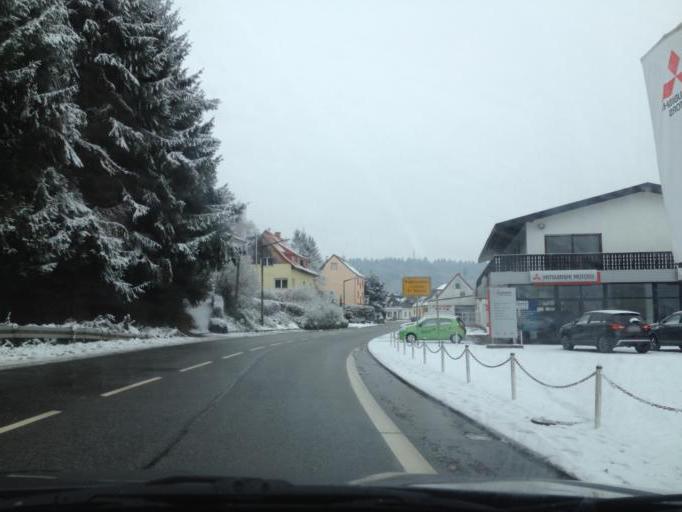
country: DE
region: Saarland
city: Ottweiler
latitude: 49.4272
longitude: 7.1627
